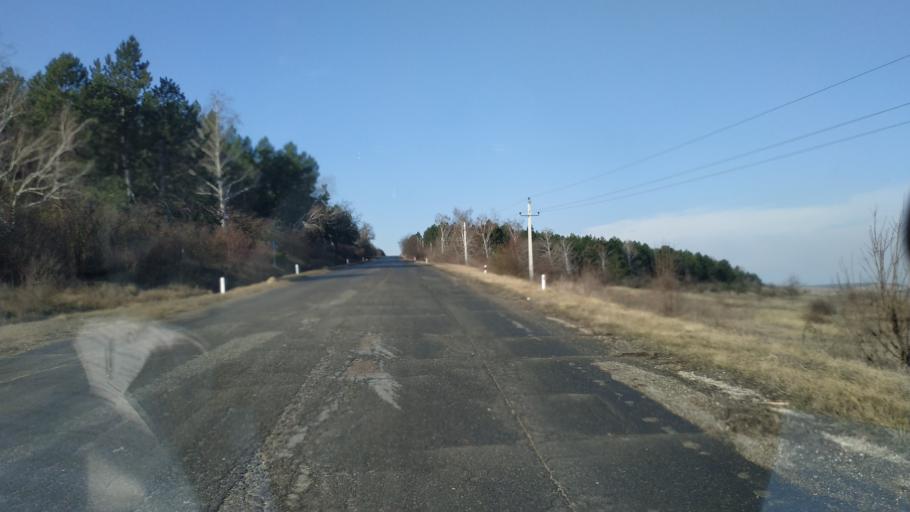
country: MD
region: Chisinau
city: Singera
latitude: 46.6973
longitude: 29.0655
